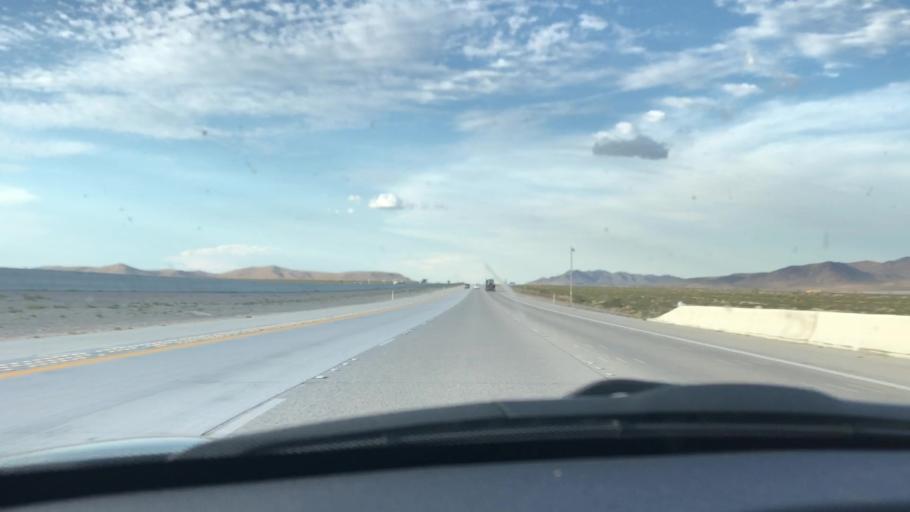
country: US
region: Nevada
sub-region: Clark County
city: Enterprise
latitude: 35.8316
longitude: -115.2879
